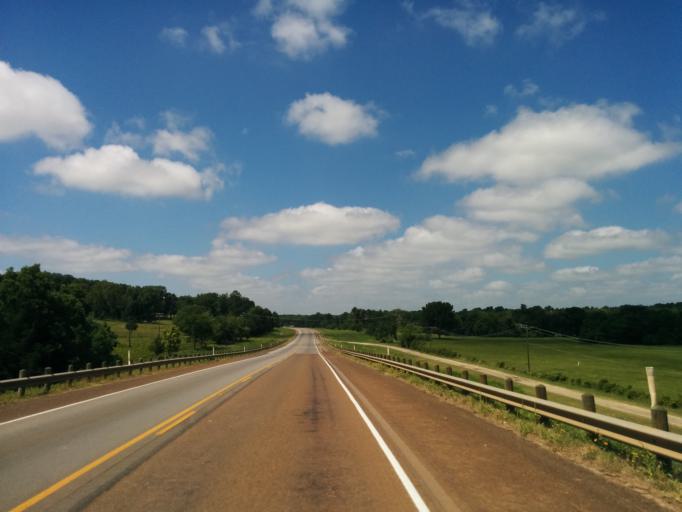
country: US
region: Texas
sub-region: Houston County
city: Crockett
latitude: 31.3310
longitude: -95.4734
